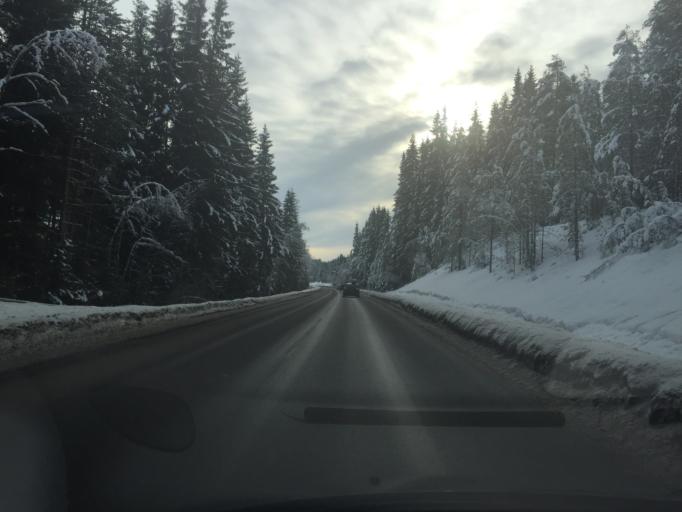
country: NO
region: Hedmark
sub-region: Trysil
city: Innbygda
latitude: 61.2784
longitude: 12.2863
